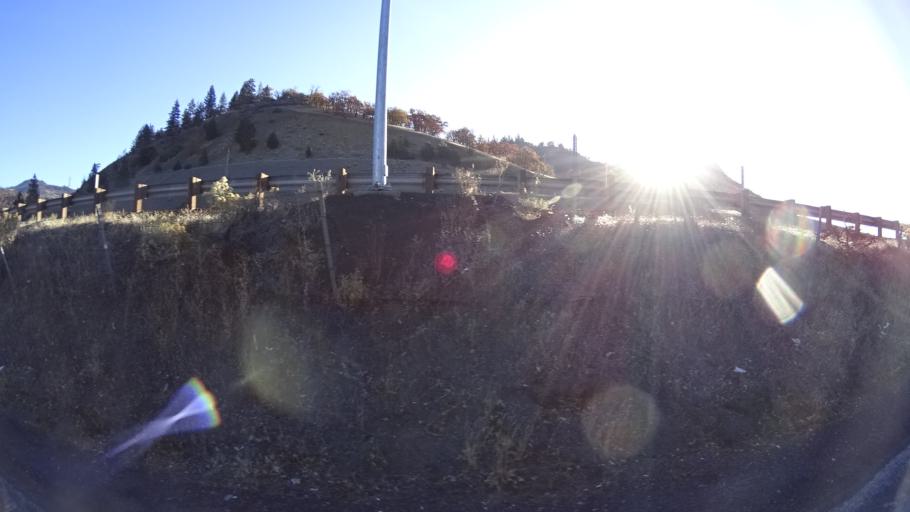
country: US
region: Oregon
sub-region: Jackson County
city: Ashland
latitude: 41.9949
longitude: -122.6109
